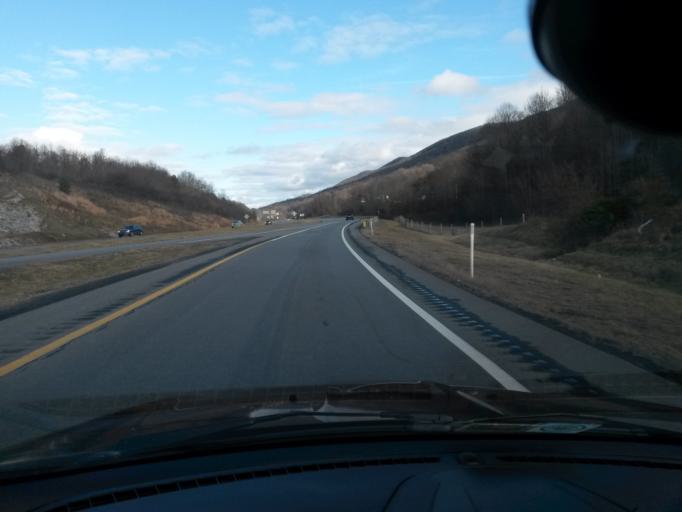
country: US
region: West Virginia
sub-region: Mercer County
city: Bluefield
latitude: 37.2734
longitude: -81.1616
